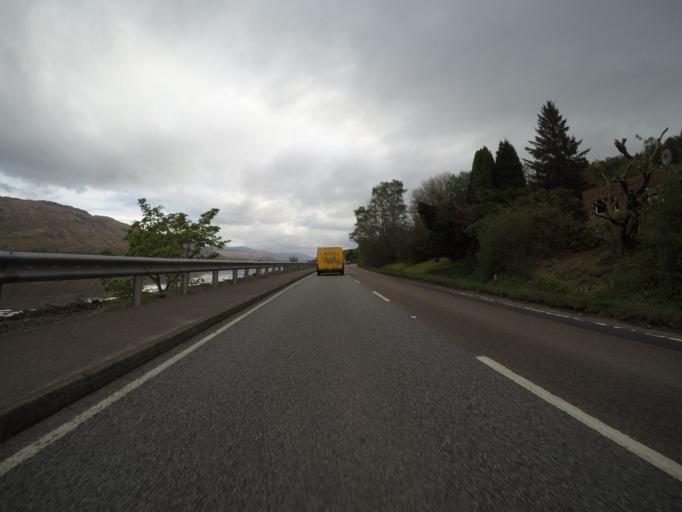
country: GB
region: Scotland
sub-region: Highland
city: Fort William
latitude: 56.7900
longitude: -5.1494
